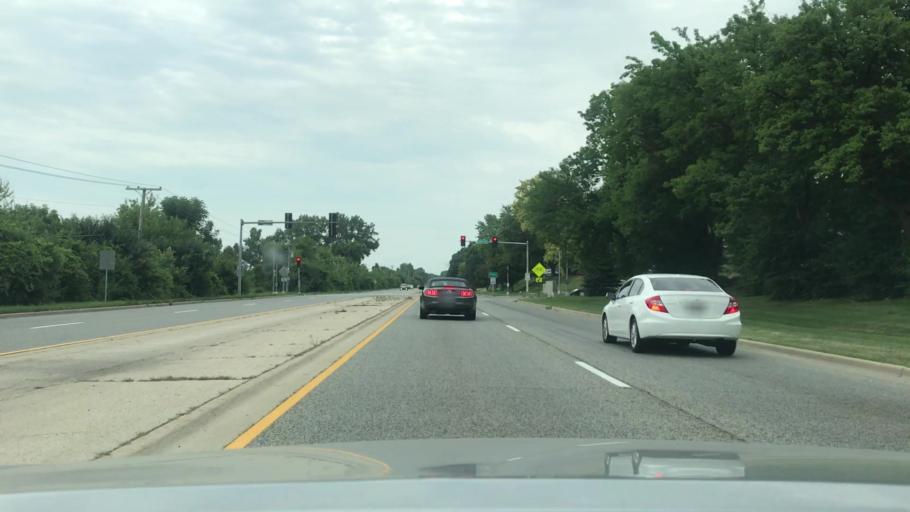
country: US
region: Illinois
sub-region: DuPage County
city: Woodridge
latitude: 41.7346
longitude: -88.0627
